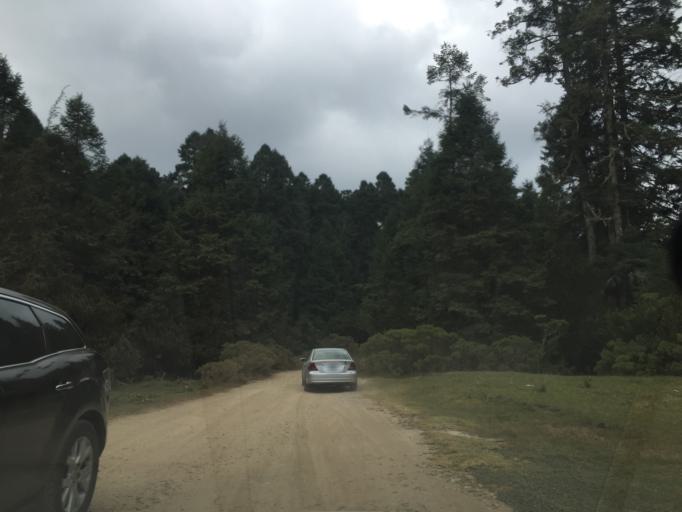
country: MX
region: Michoacan
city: Mineral de Angangueo
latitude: 19.6630
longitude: -100.2724
